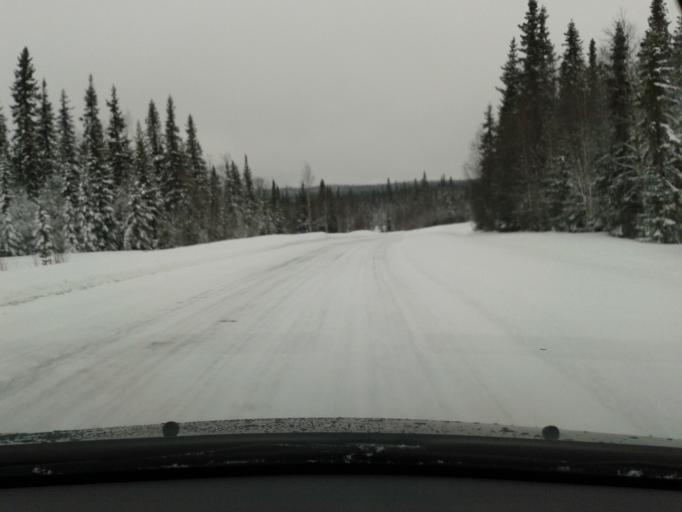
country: SE
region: Vaesterbotten
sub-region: Vilhelmina Kommun
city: Sjoberg
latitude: 65.1354
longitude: 15.8771
